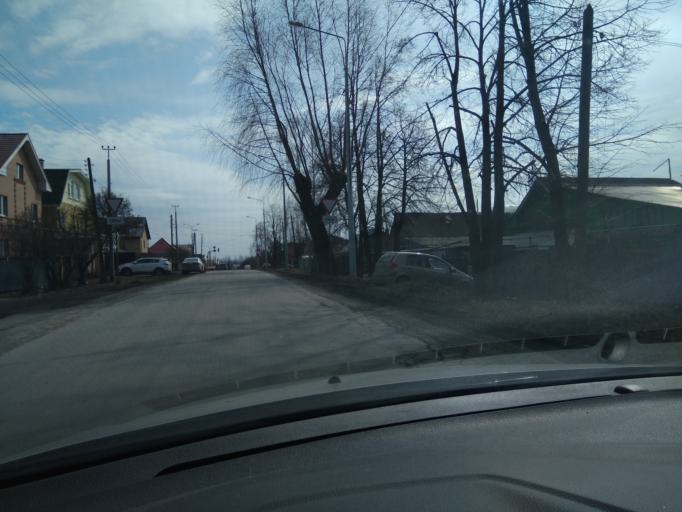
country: RU
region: Sverdlovsk
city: Shuvakish
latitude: 56.8916
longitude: 60.4848
